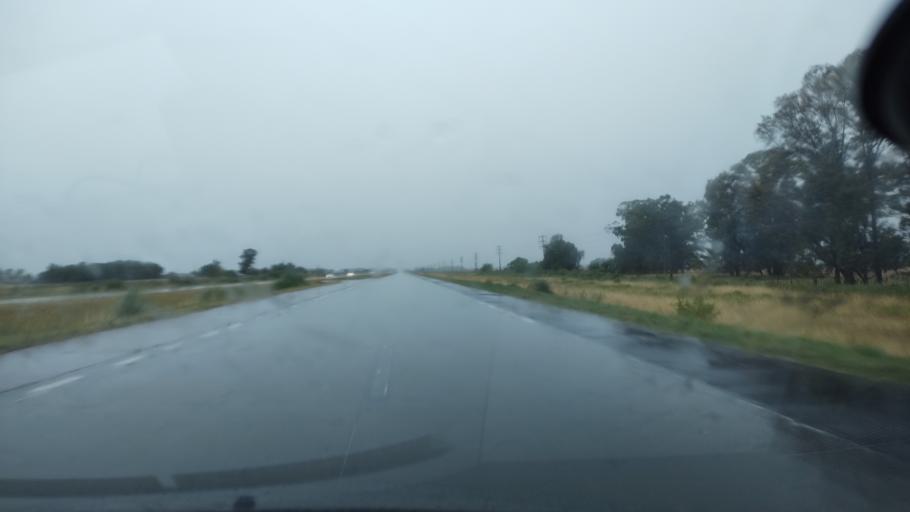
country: AR
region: Buenos Aires
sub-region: Partido de San Vicente
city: San Vicente
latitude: -35.0655
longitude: -58.4810
